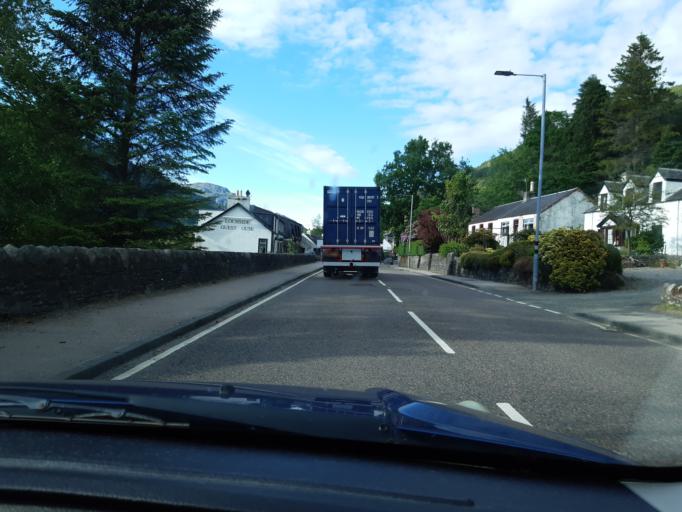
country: GB
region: Scotland
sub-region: Argyll and Bute
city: Garelochhead
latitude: 56.2016
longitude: -4.7451
